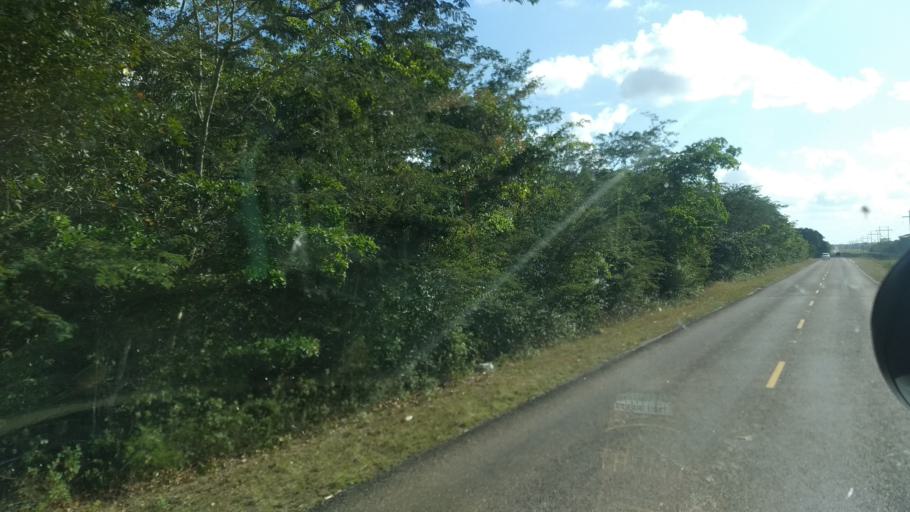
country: BZ
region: Cayo
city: Belmopan
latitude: 17.3774
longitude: -88.5257
